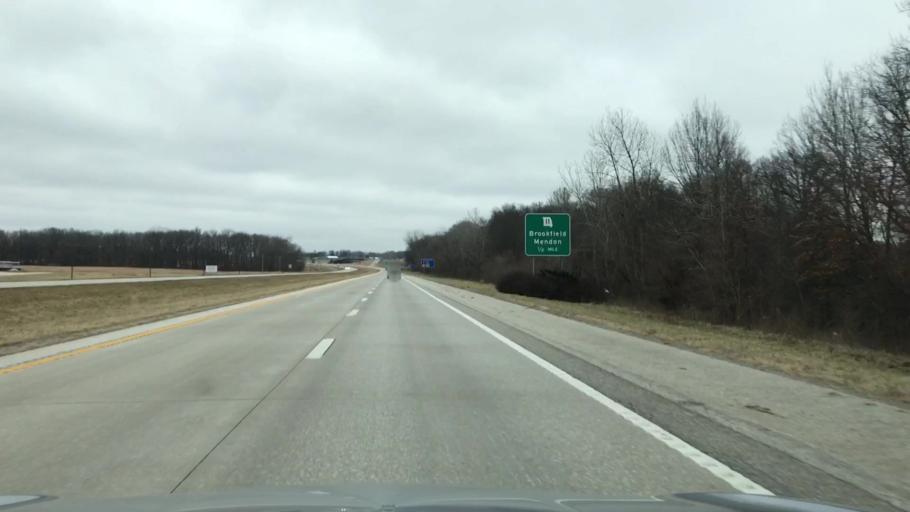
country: US
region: Missouri
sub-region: Linn County
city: Brookfield
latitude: 39.7753
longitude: -93.0888
